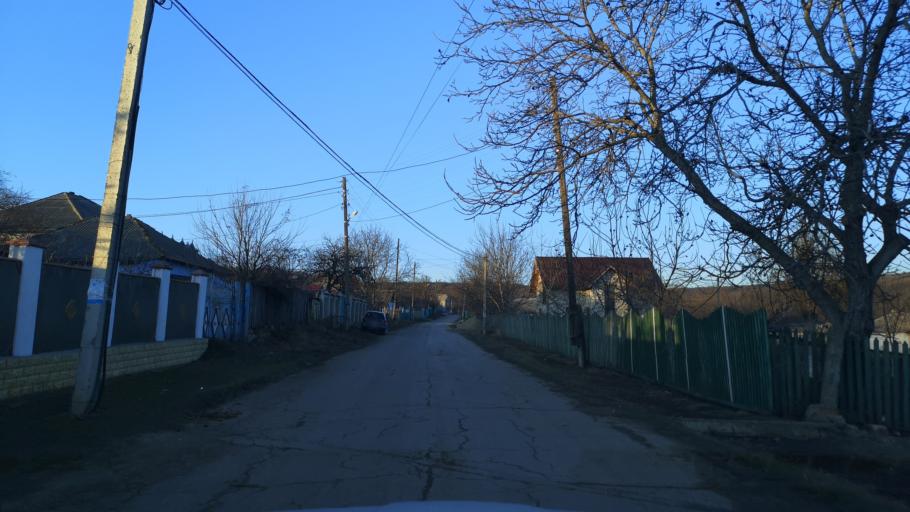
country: MD
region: Orhei
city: Orhei
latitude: 47.3613
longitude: 28.6907
